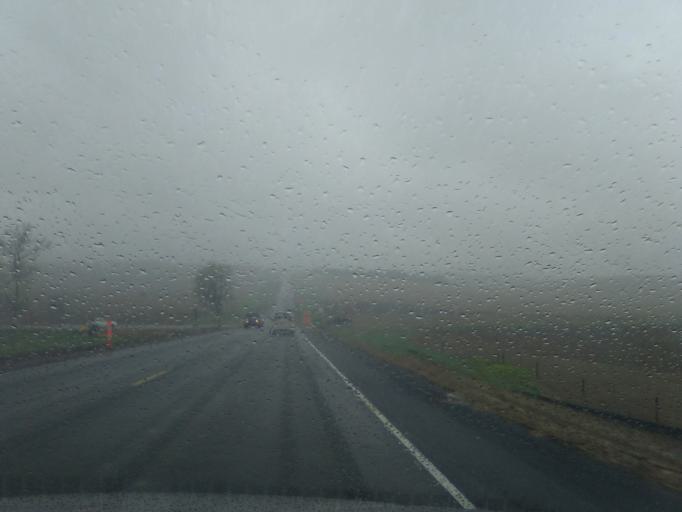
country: US
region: Nebraska
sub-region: Wayne County
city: Wayne
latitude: 42.1786
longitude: -97.1840
